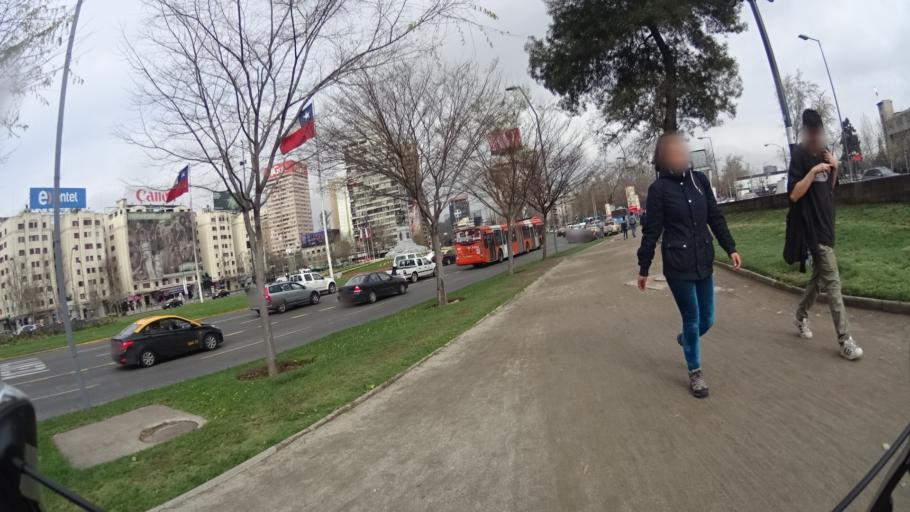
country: CL
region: Santiago Metropolitan
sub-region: Provincia de Santiago
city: Santiago
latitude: -33.4365
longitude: -70.6336
